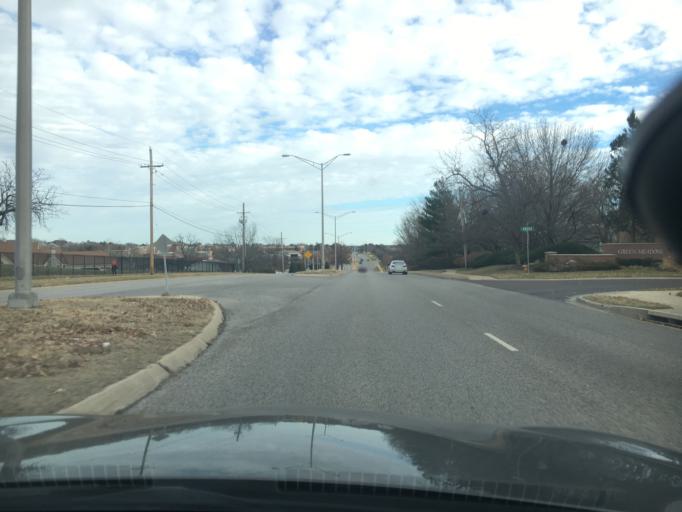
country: US
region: Kansas
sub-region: Johnson County
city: Leawood
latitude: 38.8546
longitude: -94.6530
